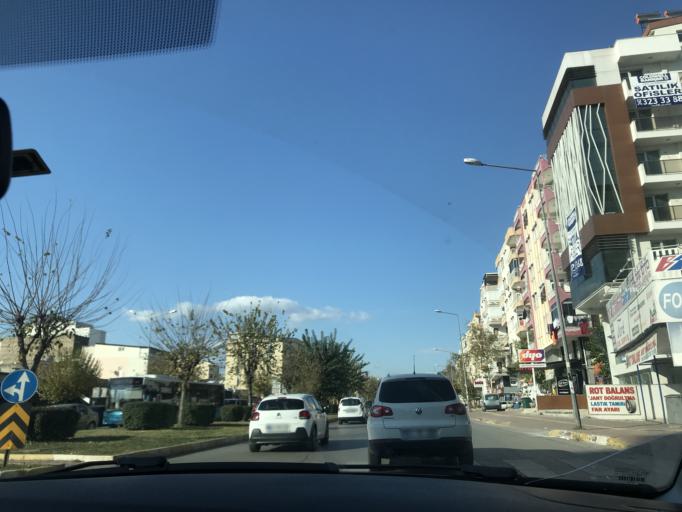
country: TR
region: Antalya
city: Antalya
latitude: 36.9073
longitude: 30.6996
